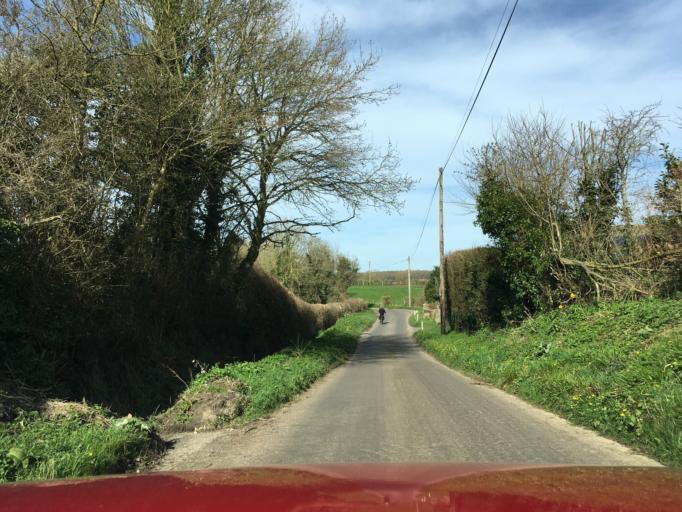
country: GB
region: England
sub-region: Wiltshire
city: Chippenham
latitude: 51.4712
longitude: -2.1503
